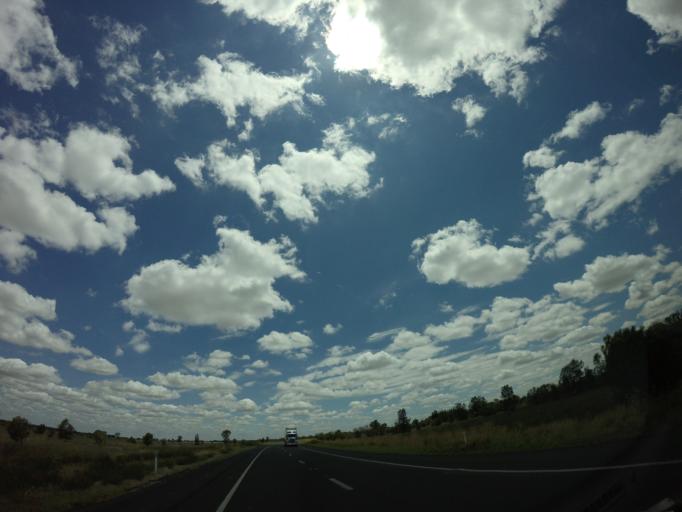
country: AU
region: New South Wales
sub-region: Moree Plains
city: Boggabilla
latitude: -29.0003
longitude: 150.0687
